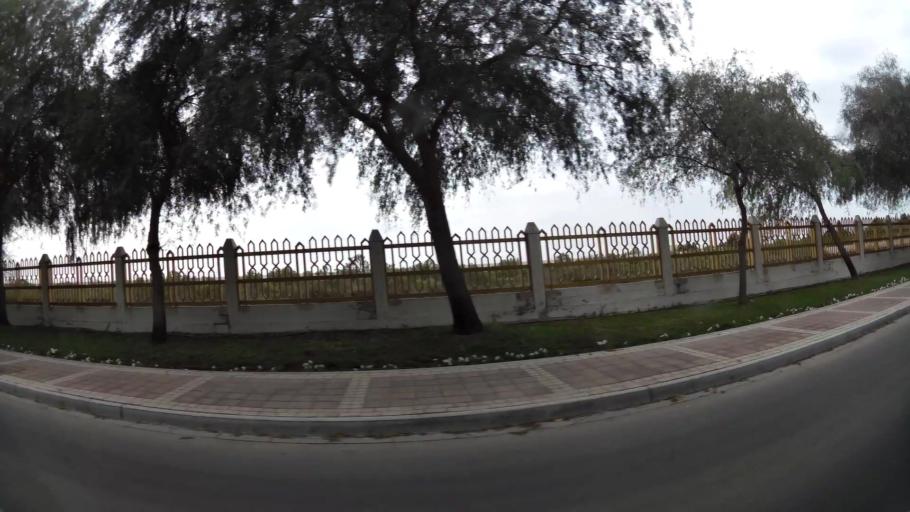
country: AE
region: Abu Dhabi
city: Abu Dhabi
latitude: 24.4265
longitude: 54.3823
